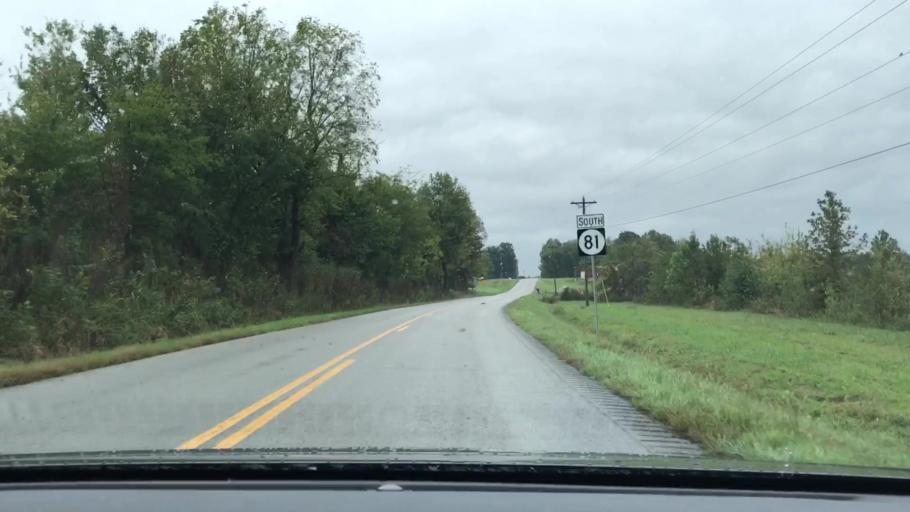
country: US
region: Kentucky
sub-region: McLean County
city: Calhoun
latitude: 37.4647
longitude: -87.2326
